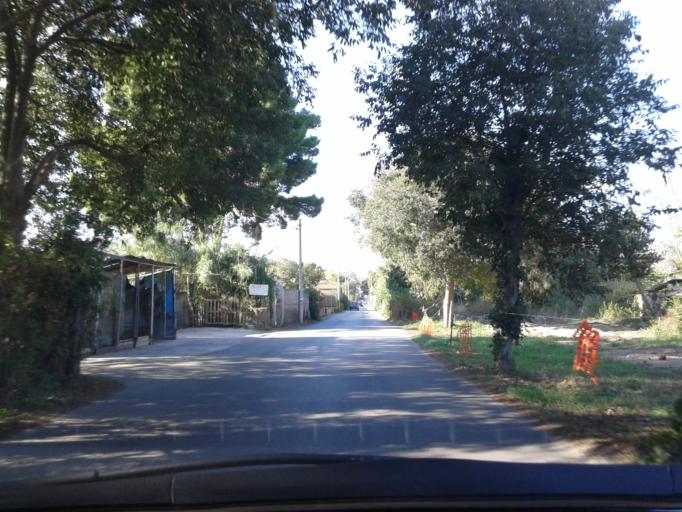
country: IT
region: Sicily
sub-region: Palermo
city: Monreale
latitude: 38.1011
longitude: 13.3162
